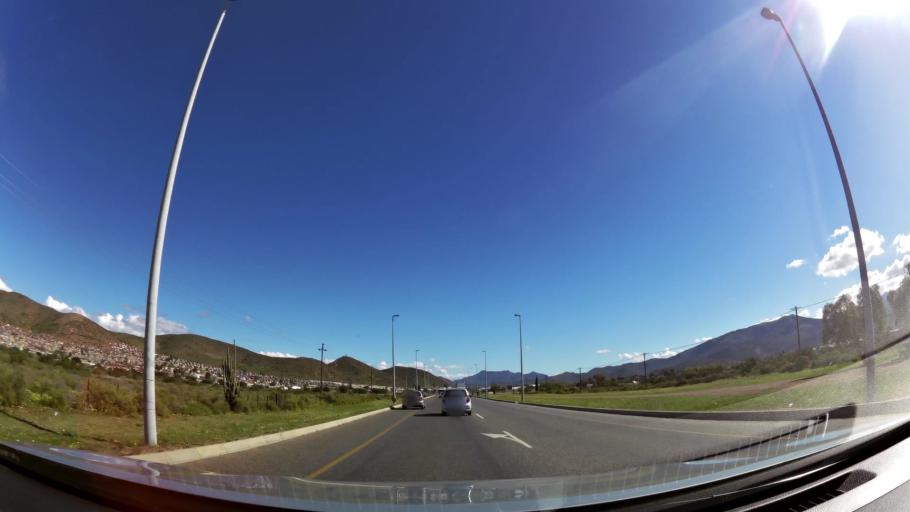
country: ZA
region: Western Cape
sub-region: Cape Winelands District Municipality
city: Ashton
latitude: -33.8148
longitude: 19.9008
